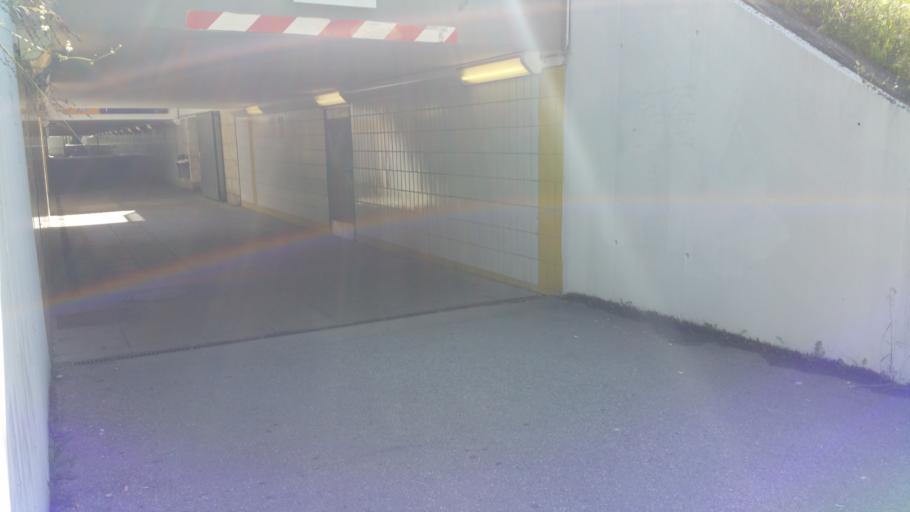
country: DE
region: Bavaria
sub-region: Upper Bavaria
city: Karlsfeld
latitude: 48.2107
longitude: 11.4595
